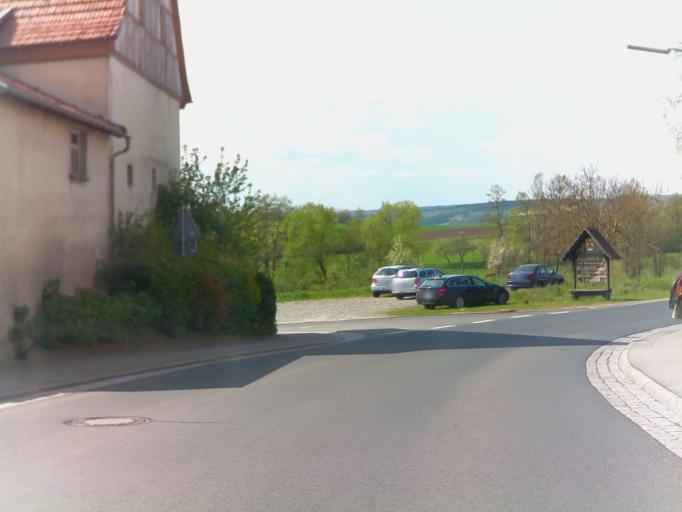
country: DE
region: Bavaria
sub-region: Regierungsbezirk Unterfranken
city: Sulzfeld
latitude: 50.2621
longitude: 10.4027
